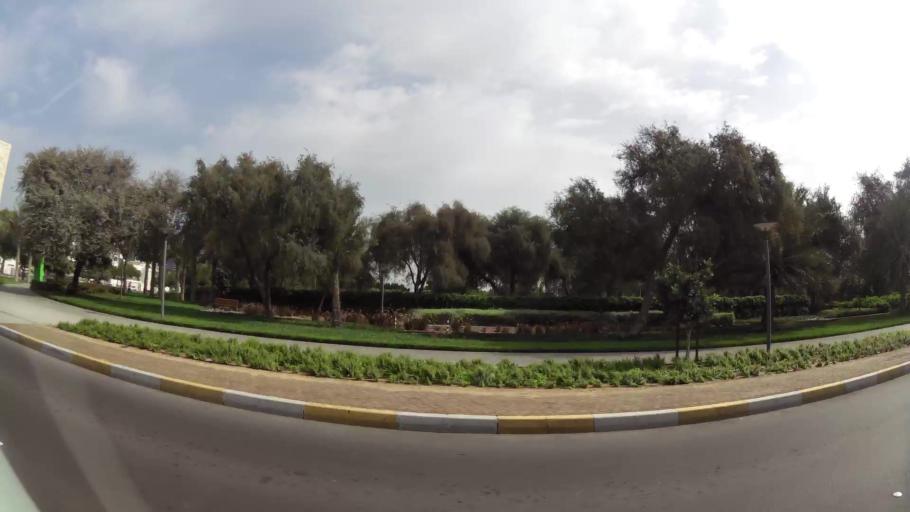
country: AE
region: Abu Dhabi
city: Abu Dhabi
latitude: 24.4534
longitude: 54.3780
